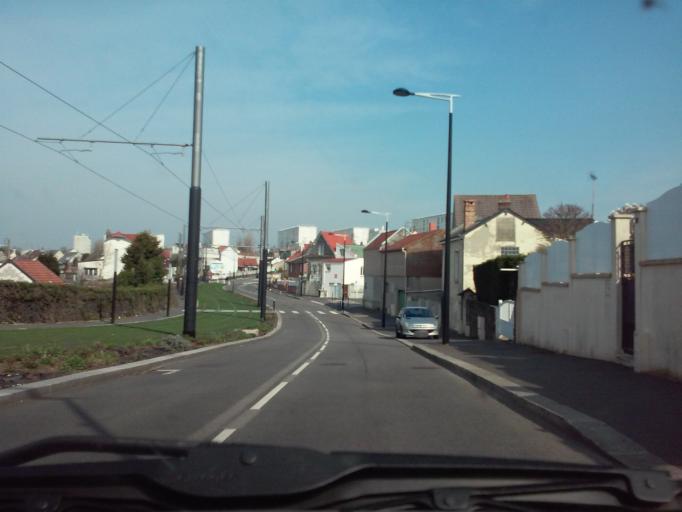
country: FR
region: Haute-Normandie
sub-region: Departement de la Seine-Maritime
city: Fontaine-la-Mallet
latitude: 49.5092
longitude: 0.1492
